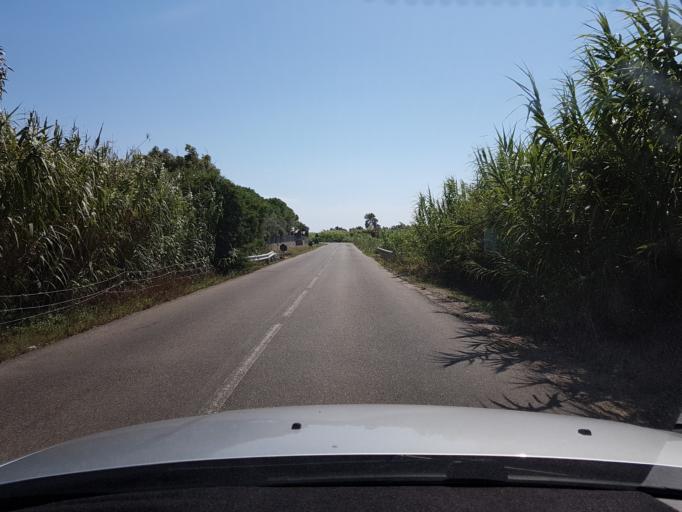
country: IT
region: Sardinia
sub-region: Provincia di Oristano
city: Nurachi
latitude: 39.9531
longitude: 8.5315
